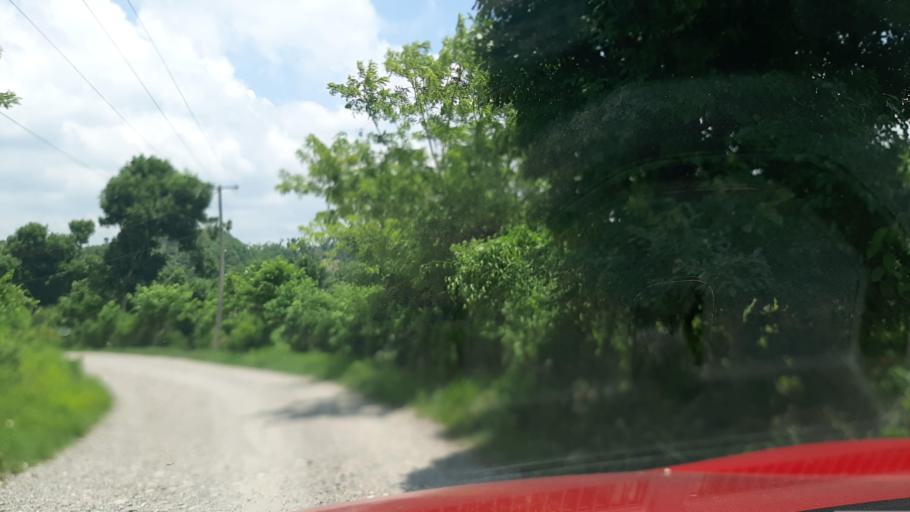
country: MX
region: Veracruz
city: Papantla de Olarte
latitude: 20.4345
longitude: -97.2687
